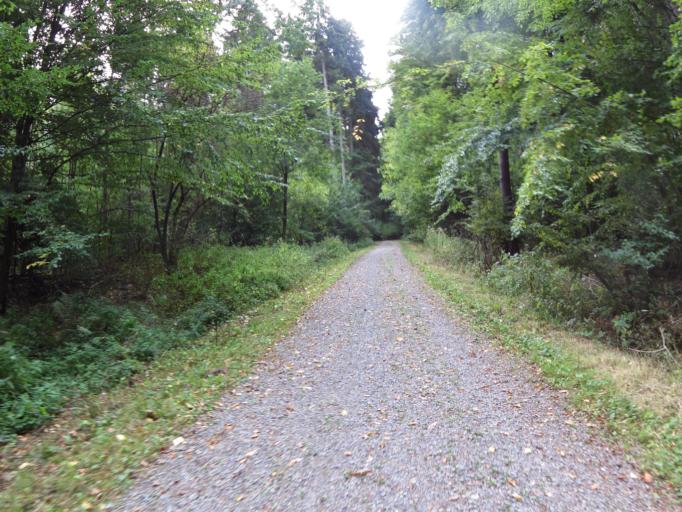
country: DE
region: Bavaria
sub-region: Regierungsbezirk Unterfranken
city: Waldbrunn
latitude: 49.7721
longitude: 9.7974
